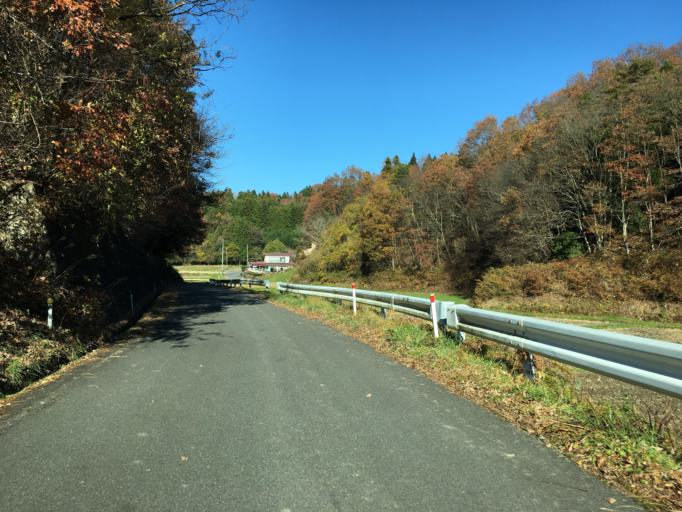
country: JP
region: Fukushima
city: Ishikawa
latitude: 37.1792
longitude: 140.5874
